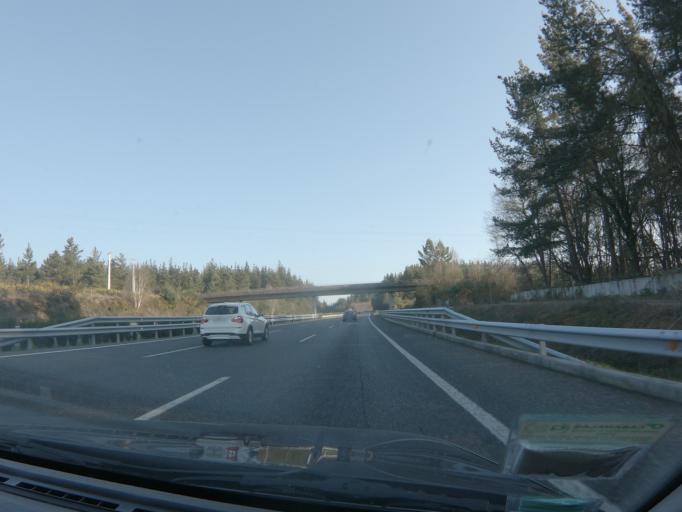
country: ES
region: Galicia
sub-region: Provincia de Lugo
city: O Paramo
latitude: 42.9273
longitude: -7.3591
